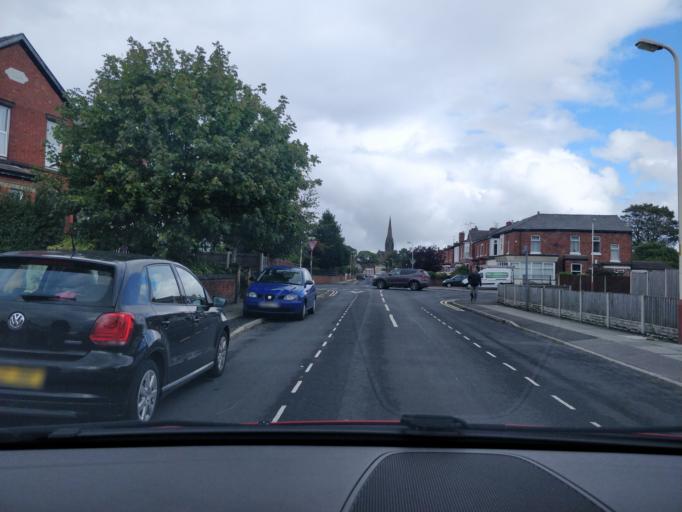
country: GB
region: England
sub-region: Sefton
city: Southport
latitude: 53.6479
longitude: -2.9895
